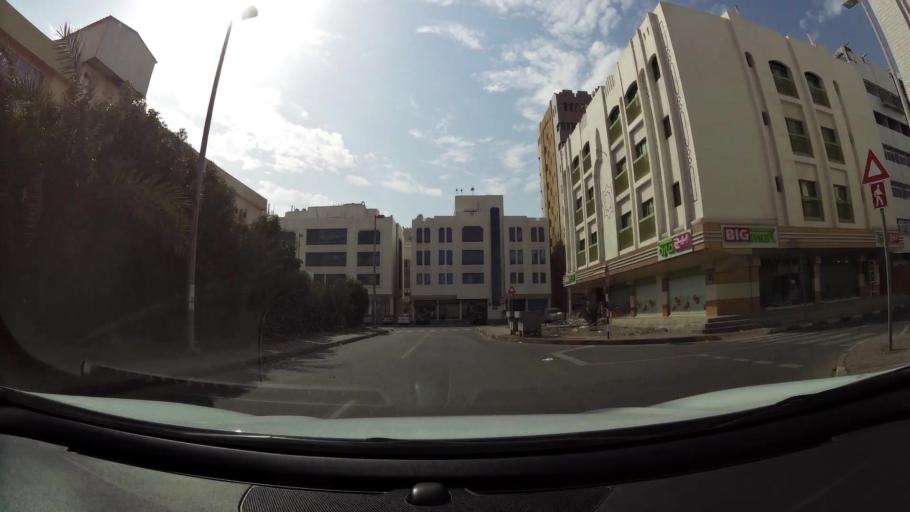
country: AE
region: Abu Dhabi
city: Abu Dhabi
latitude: 24.3274
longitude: 54.5329
